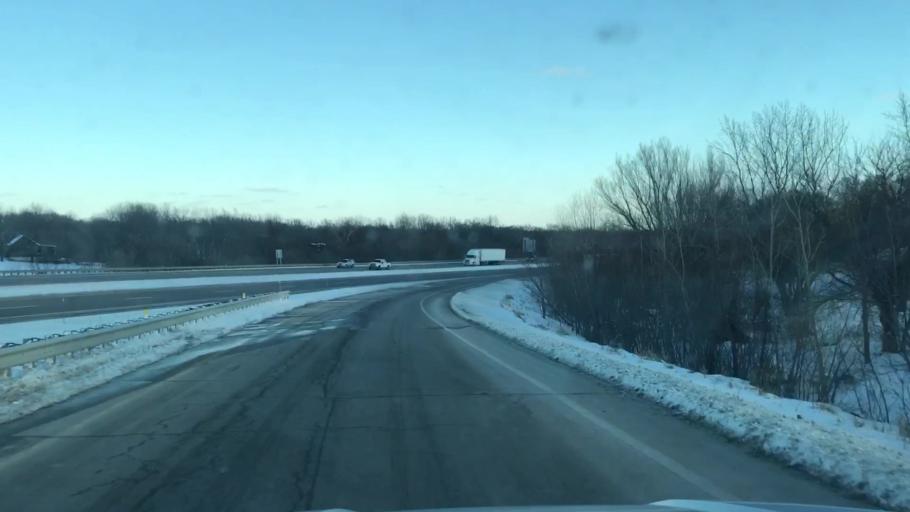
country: US
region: Missouri
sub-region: Andrew County
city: Country Club Village
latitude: 39.8565
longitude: -94.8089
